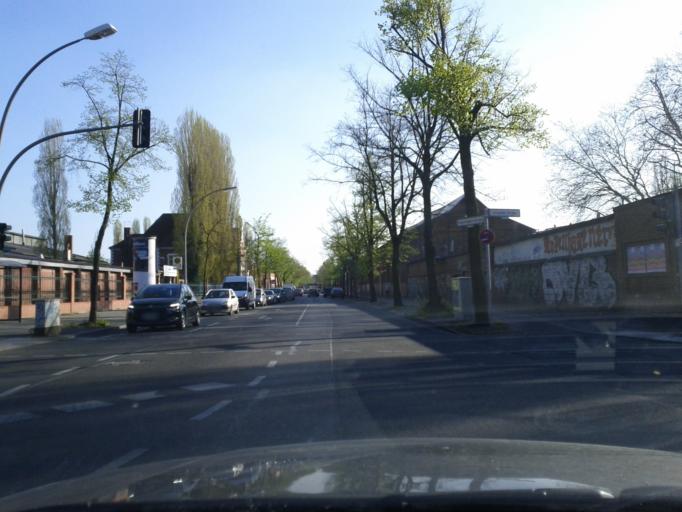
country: DE
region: Berlin
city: Wilhelmsruh
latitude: 52.5807
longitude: 13.3634
